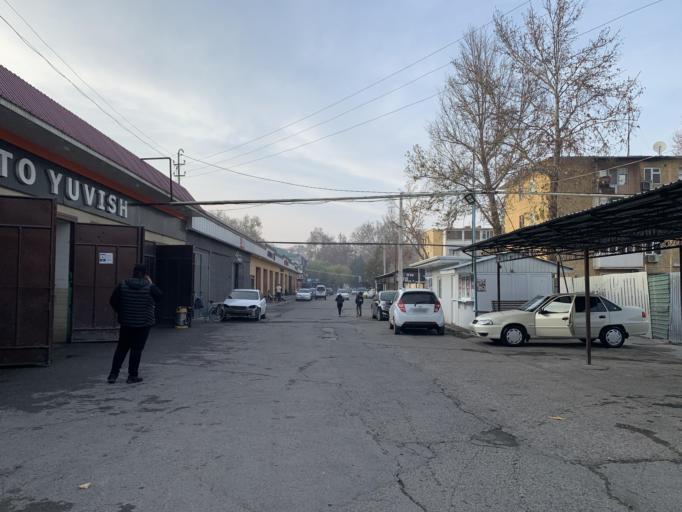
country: UZ
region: Fergana
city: Qo`qon
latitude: 40.5451
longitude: 70.9261
